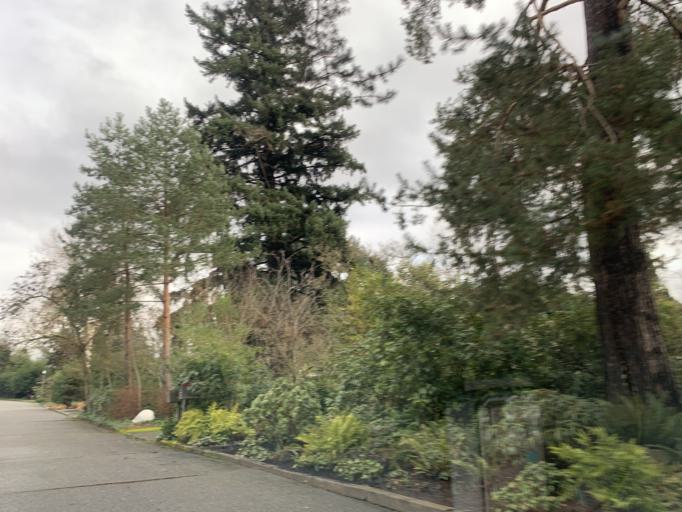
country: US
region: Washington
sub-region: King County
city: Yarrow Point
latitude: 47.6667
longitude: -122.2641
